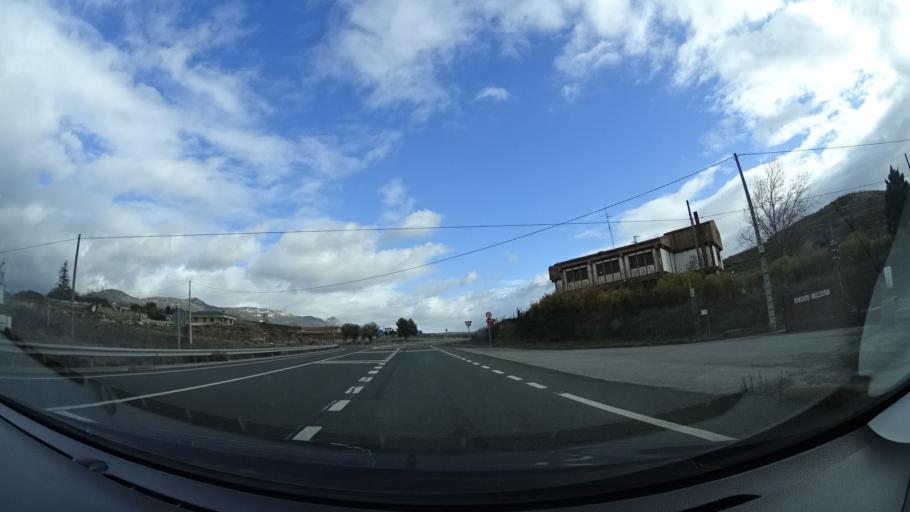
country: ES
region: La Rioja
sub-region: Provincia de La Rioja
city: San Vicente de la Sonsierra
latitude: 42.5712
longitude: -2.7596
